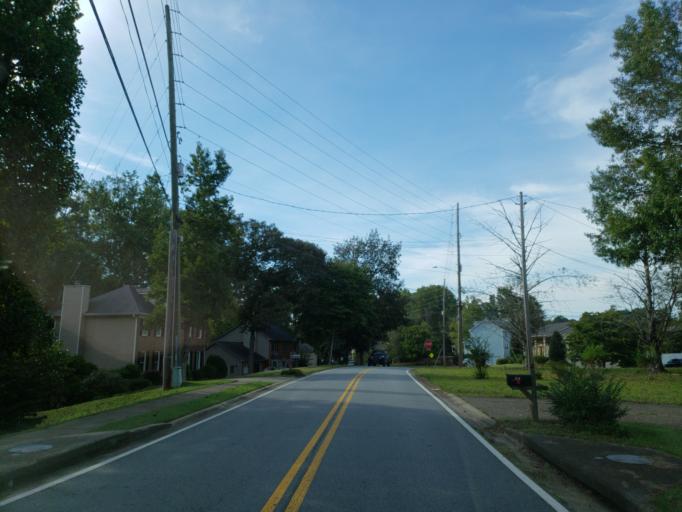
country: US
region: Georgia
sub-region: Cherokee County
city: Woodstock
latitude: 34.0661
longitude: -84.4992
